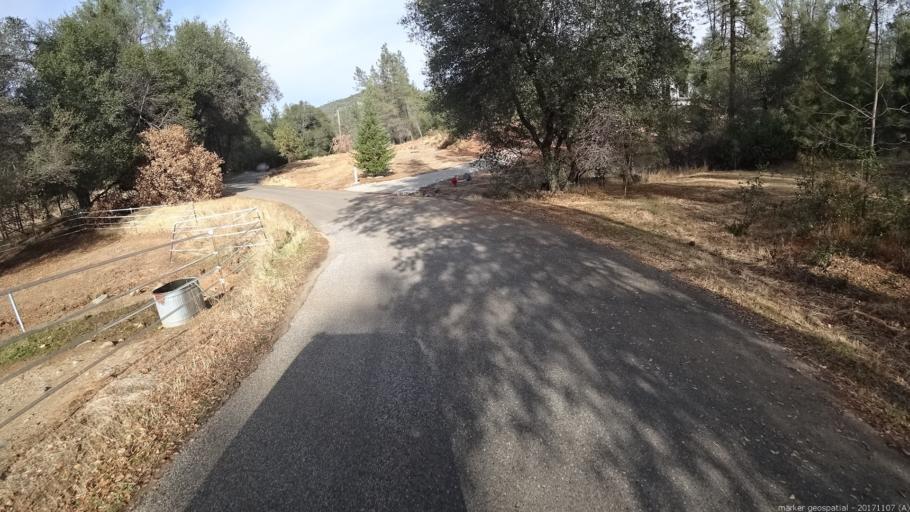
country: US
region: California
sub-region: Shasta County
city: Shasta
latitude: 40.5371
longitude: -122.5275
